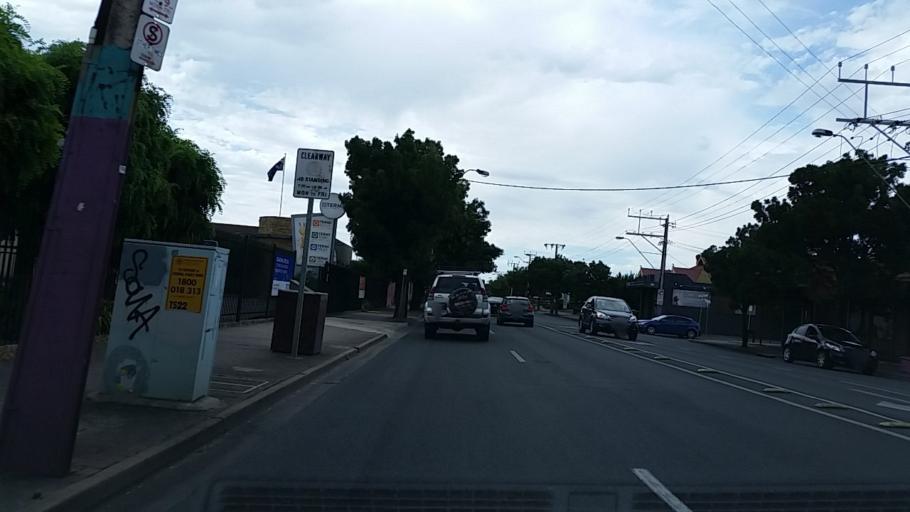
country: AU
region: South Australia
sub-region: Unley
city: Wayville
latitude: -34.9485
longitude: 138.5894
